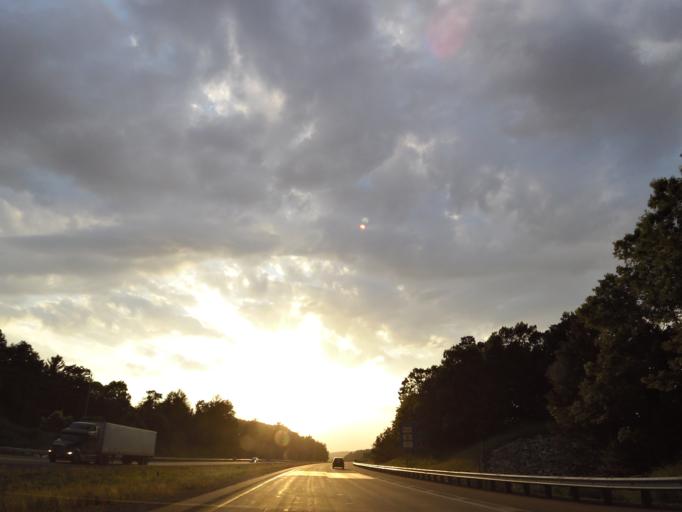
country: US
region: Wisconsin
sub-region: Eau Claire County
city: Eau Claire
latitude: 44.7698
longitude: -91.5094
